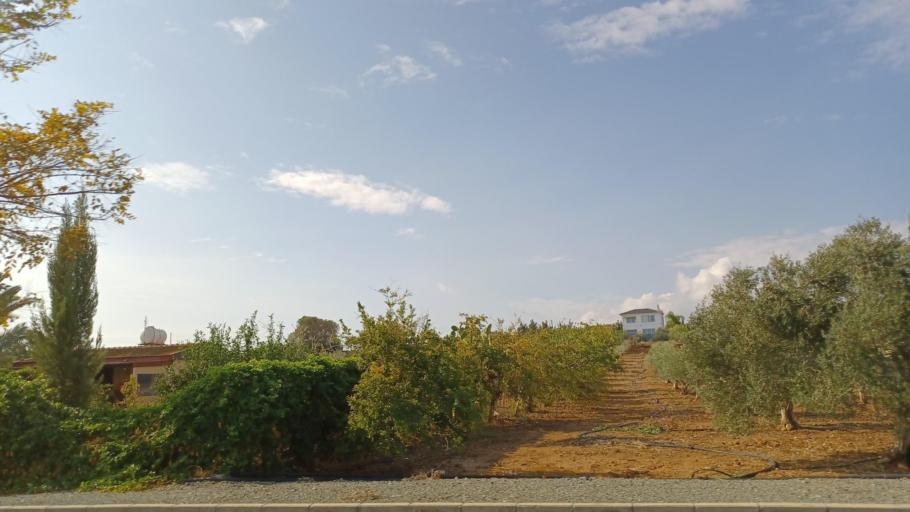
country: CY
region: Larnaka
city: Tersefanou
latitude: 34.7890
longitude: 33.4923
